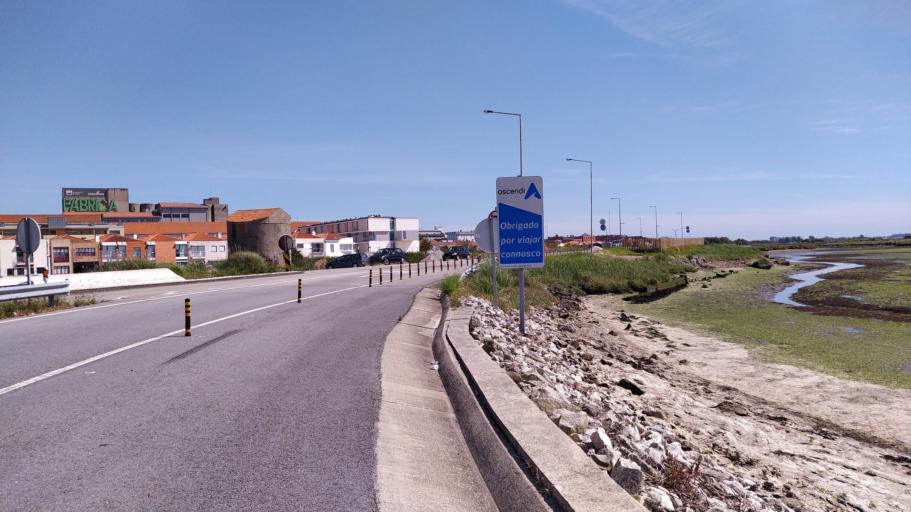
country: PT
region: Aveiro
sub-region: Aveiro
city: Aveiro
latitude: 40.6402
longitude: -8.6594
